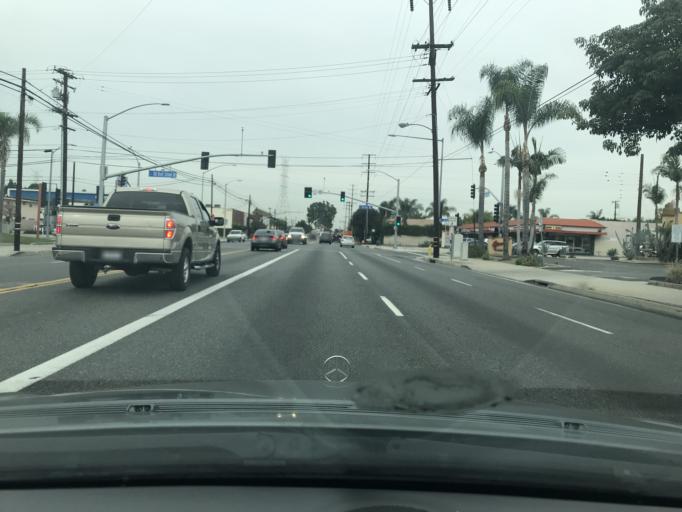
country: US
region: California
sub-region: Los Angeles County
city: Bell Gardens
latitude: 33.9586
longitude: -118.1399
